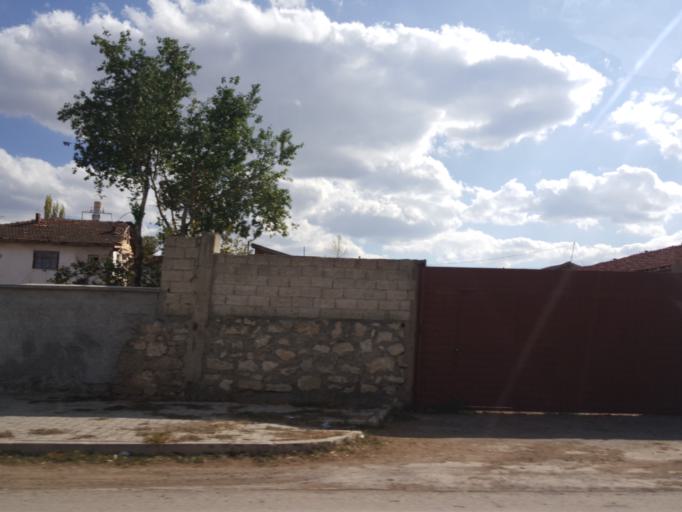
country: TR
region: Tokat
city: Yesilyurt
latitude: 40.0079
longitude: 36.2071
